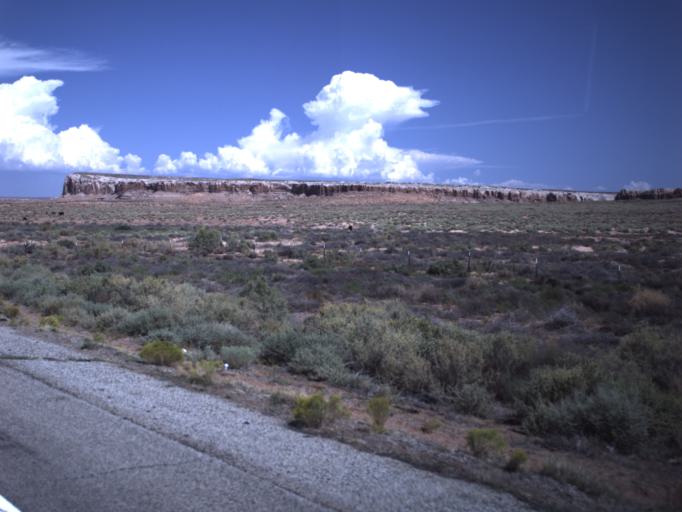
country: US
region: Utah
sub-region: San Juan County
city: Blanding
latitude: 37.2070
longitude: -109.6081
